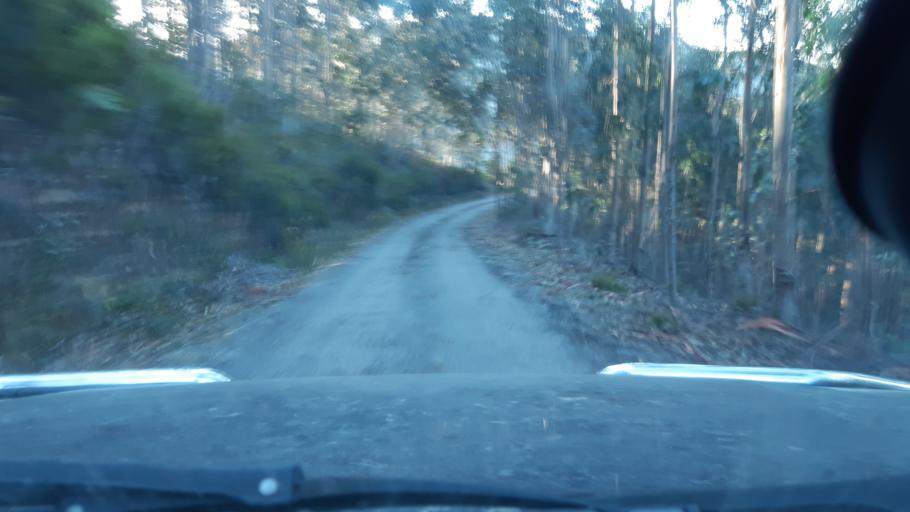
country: PT
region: Viseu
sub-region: Mortagua
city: Mortagua
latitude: 40.5233
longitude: -8.2530
